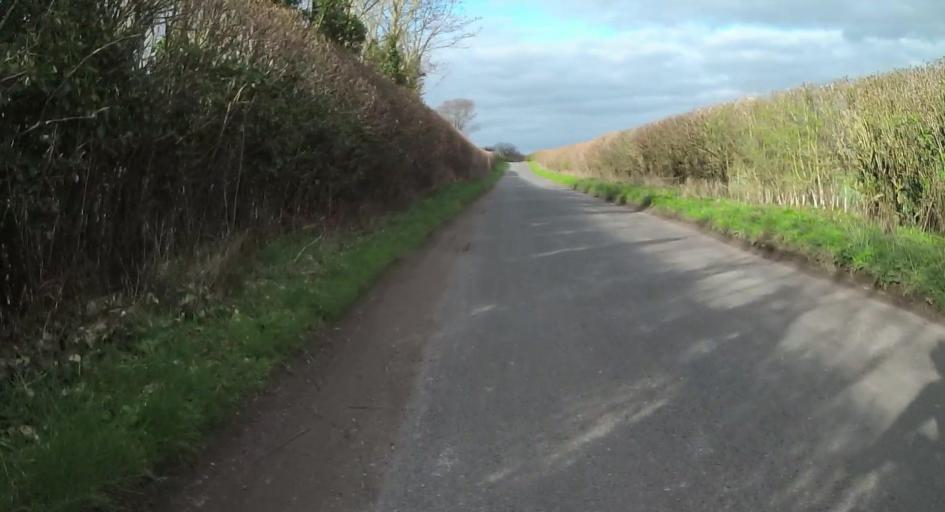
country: GB
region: England
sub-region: Hampshire
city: Andover
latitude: 51.1593
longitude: -1.4880
